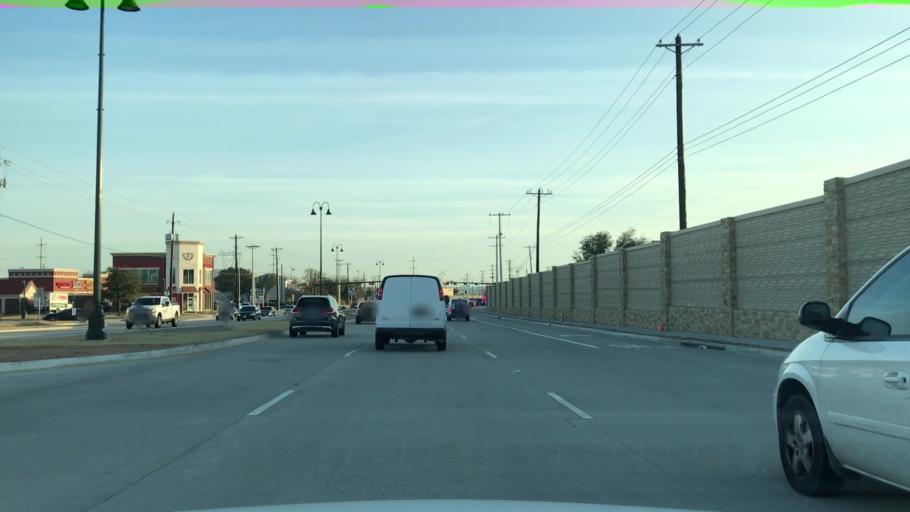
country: US
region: Texas
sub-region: Denton County
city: The Colony
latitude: 33.0760
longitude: -96.8929
